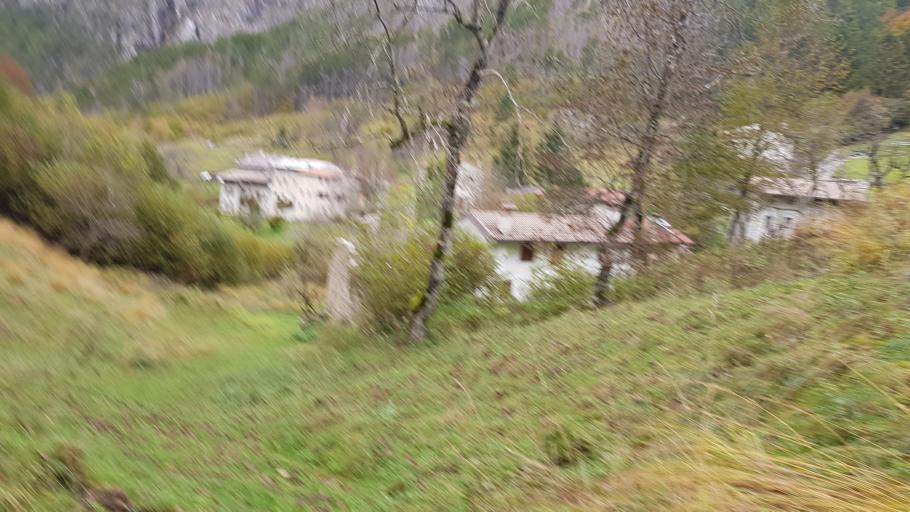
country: IT
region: Friuli Venezia Giulia
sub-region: Provincia di Udine
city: Chiusaforte
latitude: 46.4062
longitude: 13.3495
